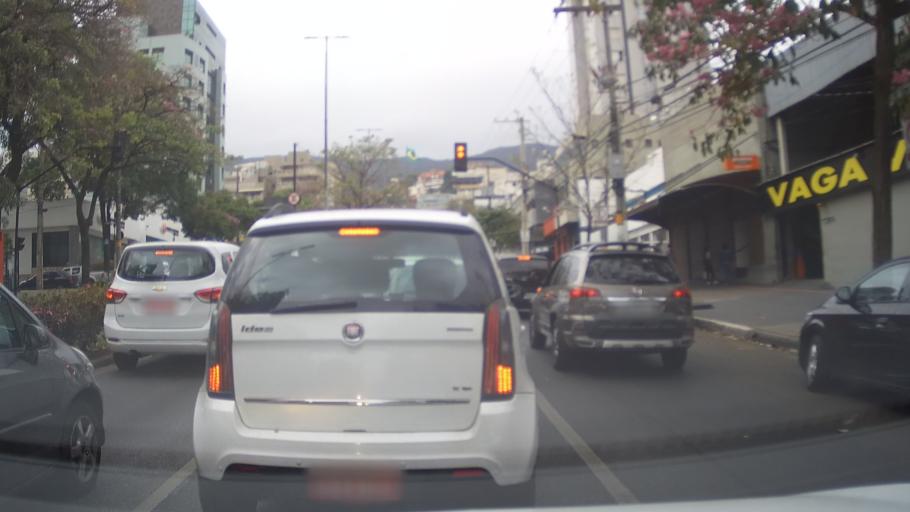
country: BR
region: Minas Gerais
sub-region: Belo Horizonte
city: Belo Horizonte
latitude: -19.9466
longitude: -43.9215
